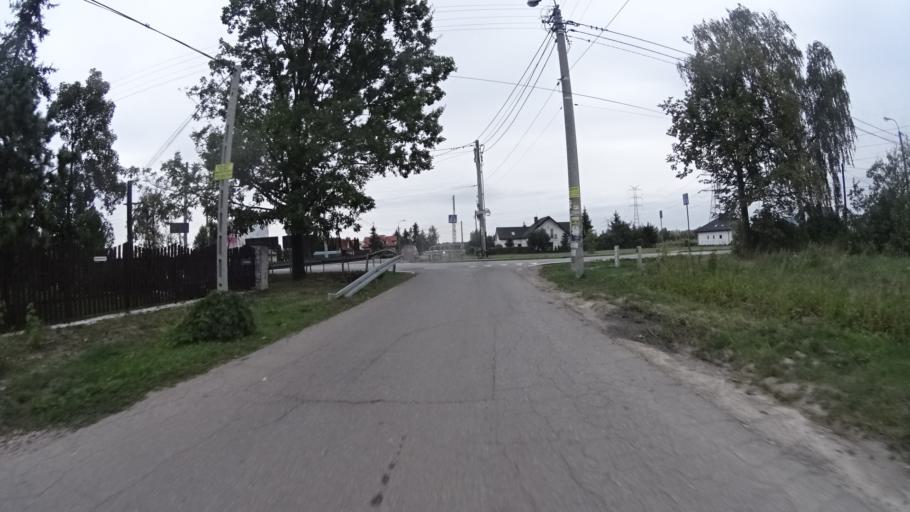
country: PL
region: Masovian Voivodeship
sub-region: Powiat warszawski zachodni
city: Stare Babice
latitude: 52.2640
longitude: 20.8241
